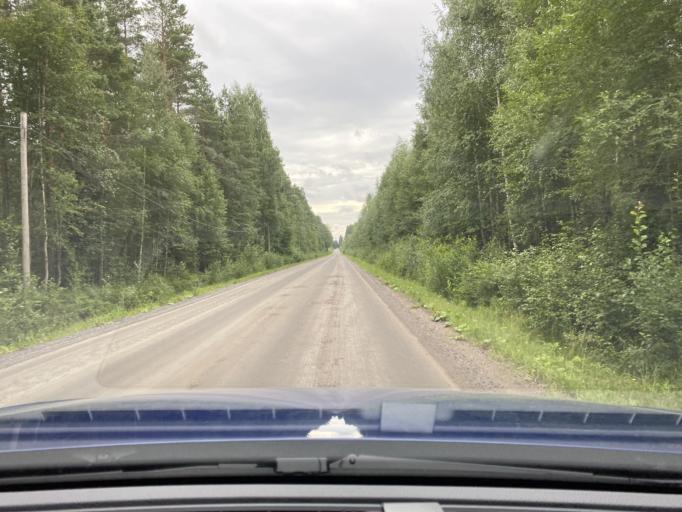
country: FI
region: Satakunta
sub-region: Rauma
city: Kiukainen
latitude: 61.1428
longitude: 21.9966
